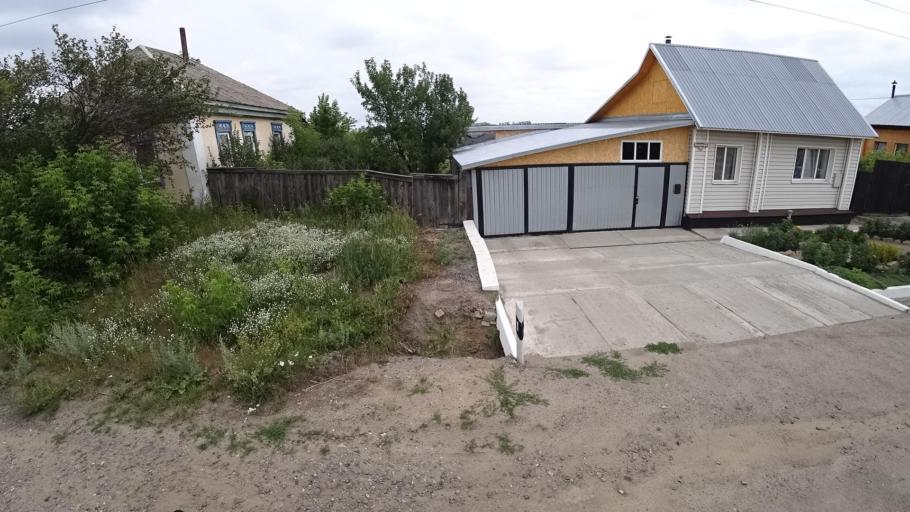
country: RU
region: Sverdlovsk
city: Kamyshlov
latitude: 56.8513
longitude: 62.6788
